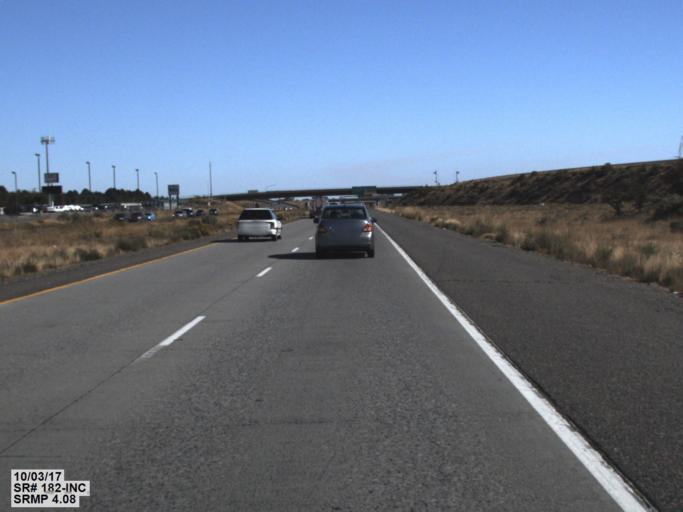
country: US
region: Washington
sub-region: Benton County
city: Richland
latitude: 46.2587
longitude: -119.2807
